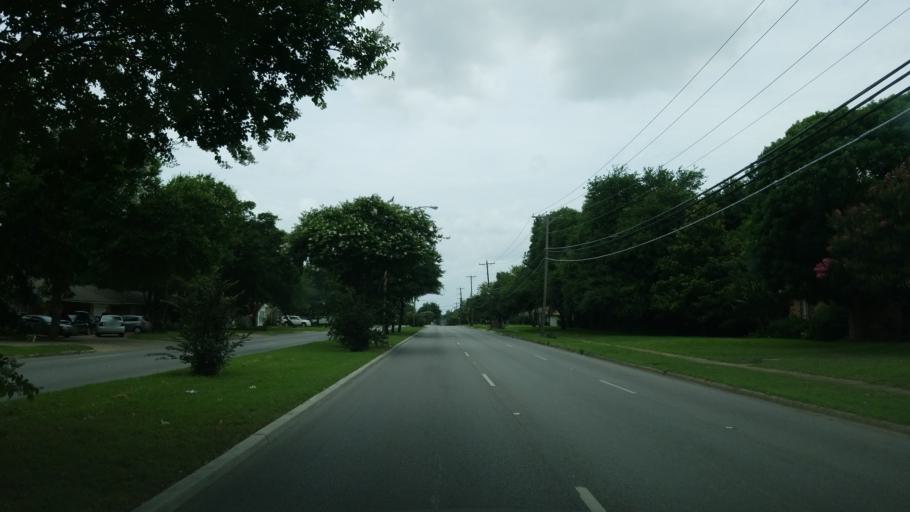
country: US
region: Texas
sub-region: Dallas County
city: Farmers Branch
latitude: 32.8809
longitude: -96.8695
